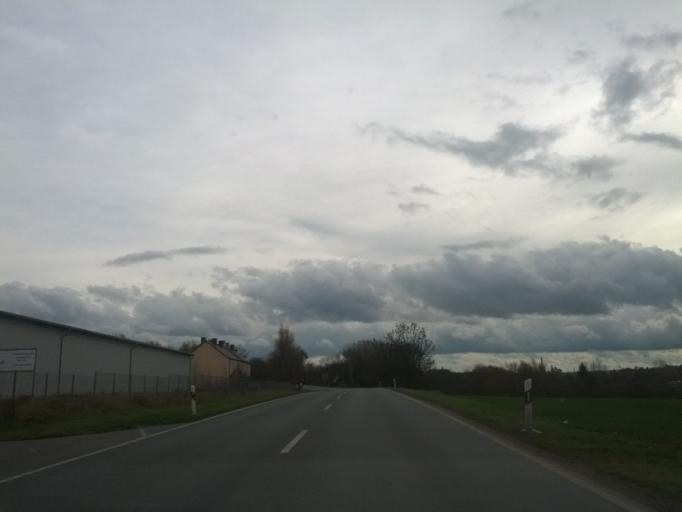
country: DE
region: Thuringia
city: Remstadt
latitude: 50.9706
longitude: 10.6989
